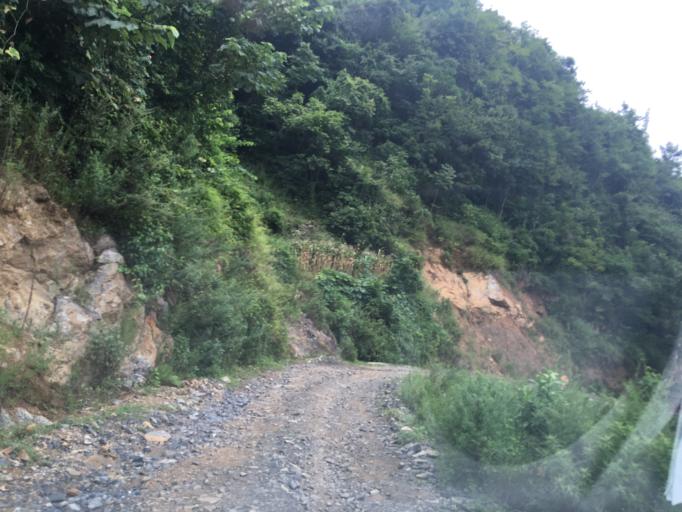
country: CN
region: Guangxi Zhuangzu Zizhiqu
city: Xinzhou
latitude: 25.1718
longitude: 105.7315
